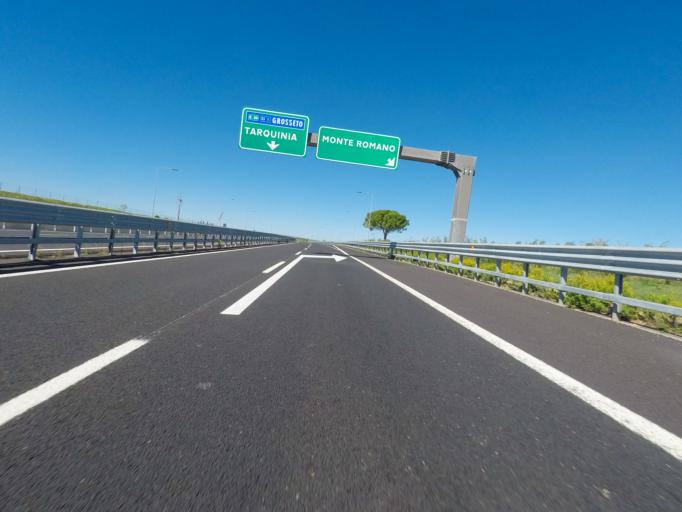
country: IT
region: Latium
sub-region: Provincia di Viterbo
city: Tarquinia
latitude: 42.2073
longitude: 11.7833
